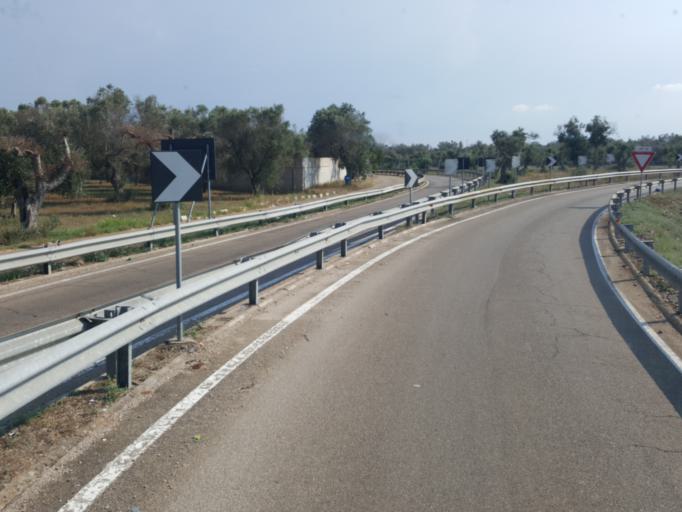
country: IT
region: Apulia
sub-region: Provincia di Lecce
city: Trepuzzi
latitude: 40.4396
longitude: 18.0806
